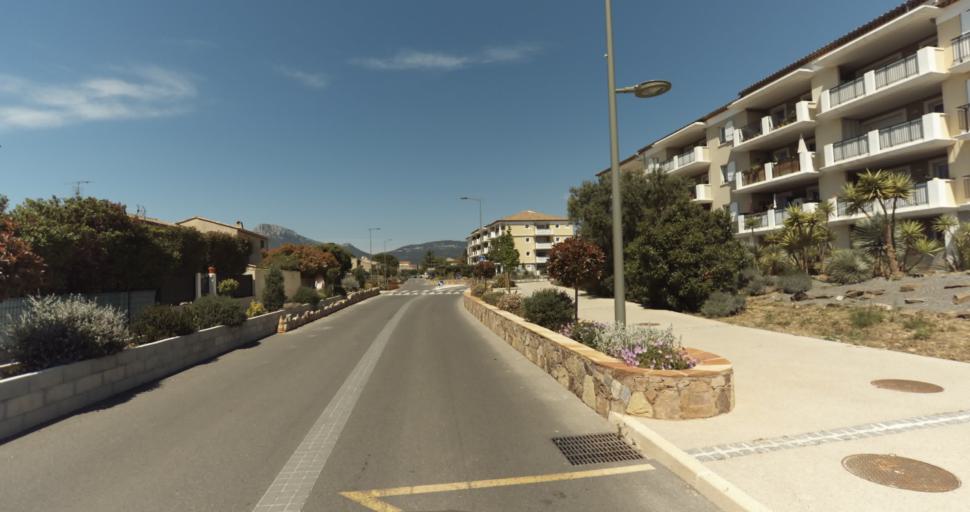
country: FR
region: Provence-Alpes-Cote d'Azur
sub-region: Departement du Var
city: La Crau
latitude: 43.1448
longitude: 6.0739
